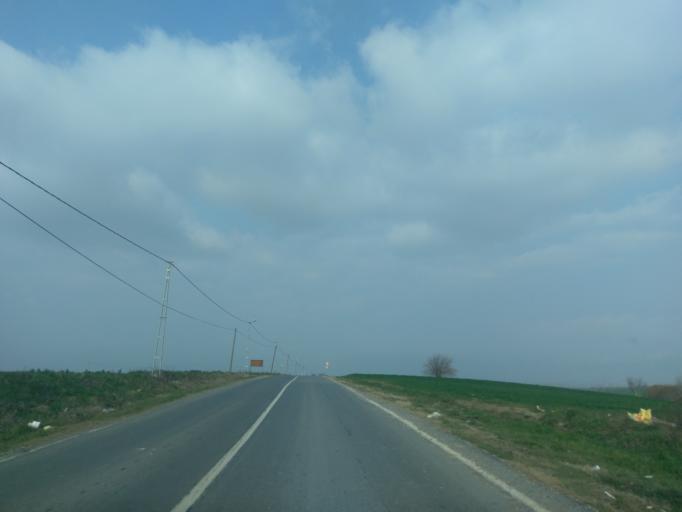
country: TR
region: Istanbul
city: Silivri
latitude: 41.0860
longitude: 28.2669
